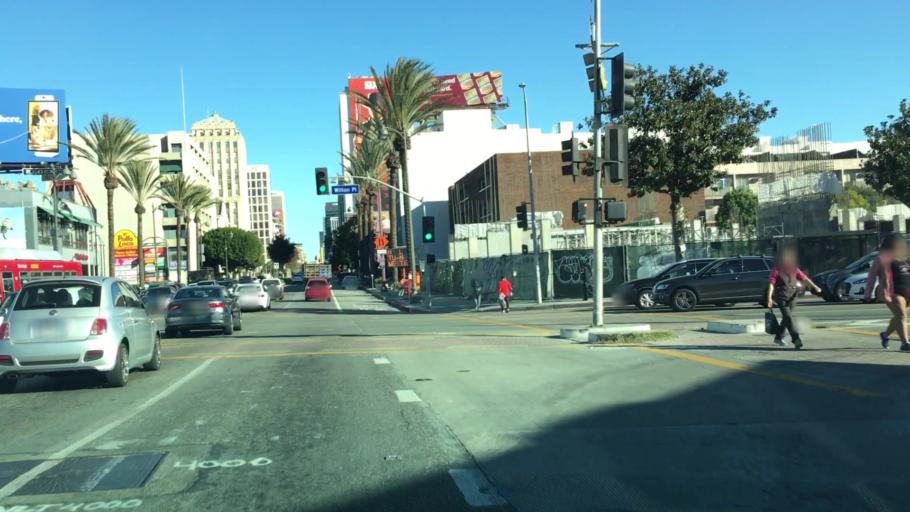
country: US
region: California
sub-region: Los Angeles County
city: Hollywood
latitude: 34.0617
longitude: -118.3145
